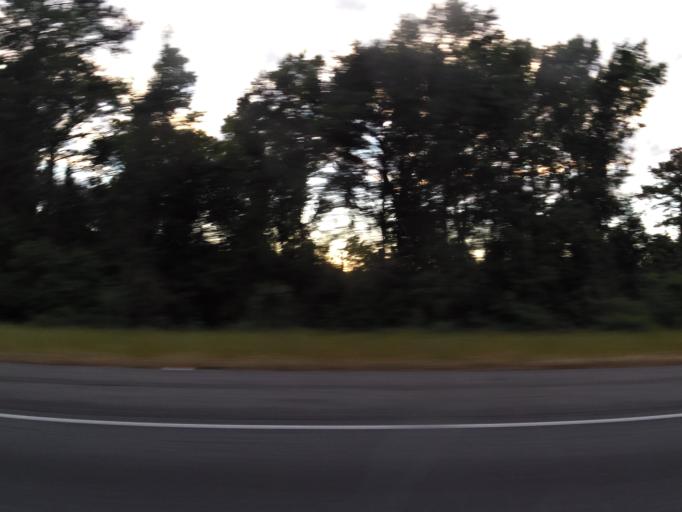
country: US
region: Georgia
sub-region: Chatham County
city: Georgetown
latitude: 32.0264
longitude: -81.2702
